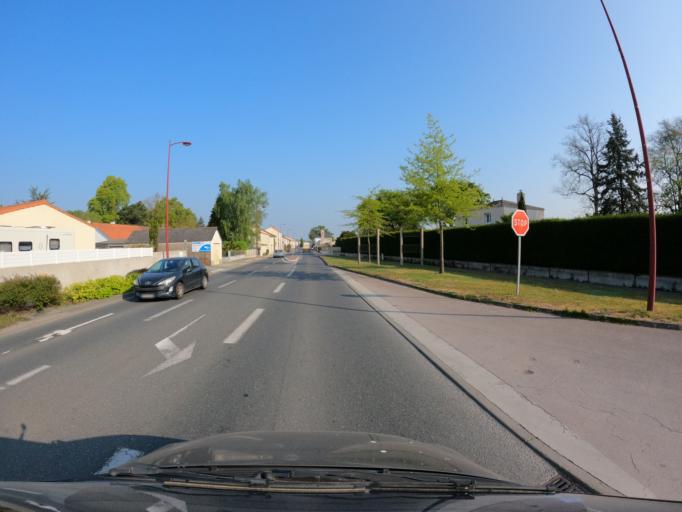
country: FR
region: Pays de la Loire
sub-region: Departement de la Loire-Atlantique
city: Geneston
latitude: 47.0520
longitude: -1.5096
